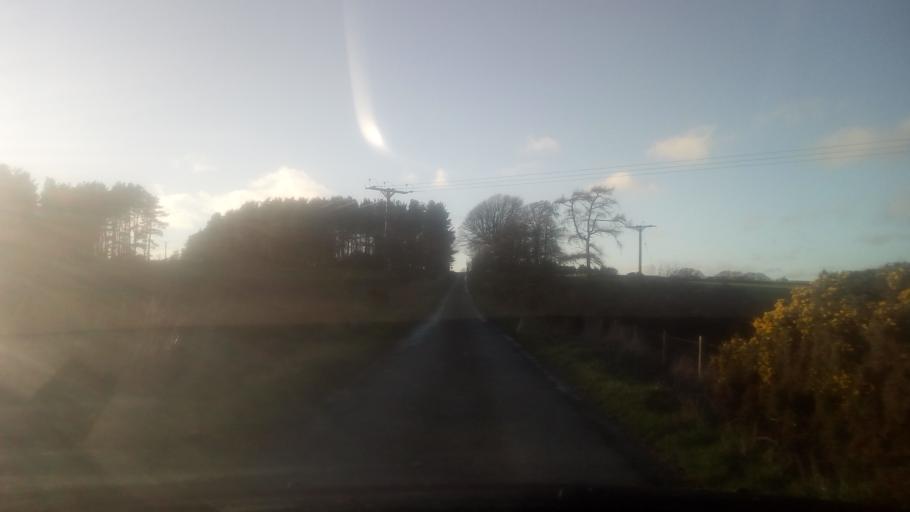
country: GB
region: Scotland
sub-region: The Scottish Borders
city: Jedburgh
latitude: 55.4716
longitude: -2.4475
